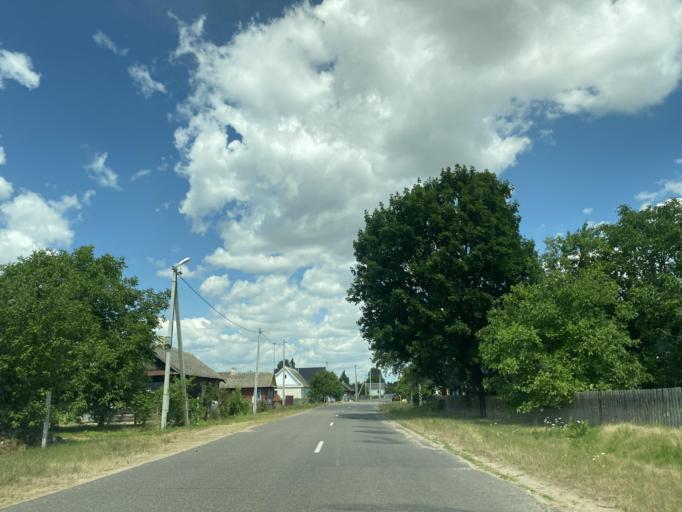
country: BY
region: Brest
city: Ivanava
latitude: 52.1687
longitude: 25.5592
